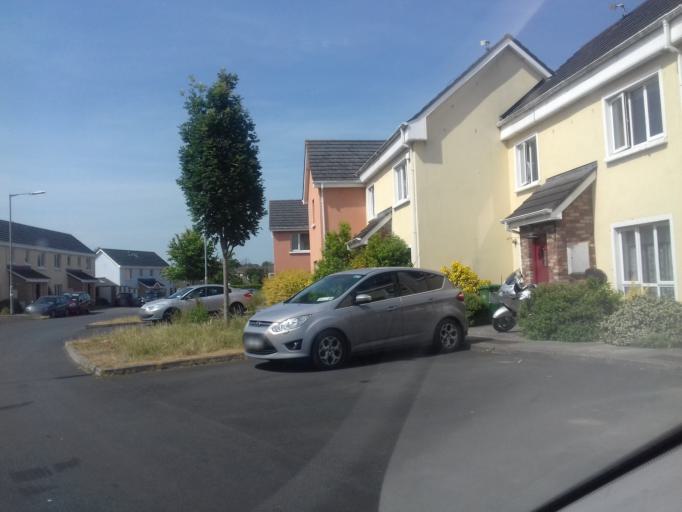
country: IE
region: Leinster
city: Lusk
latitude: 53.5246
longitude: -6.1715
